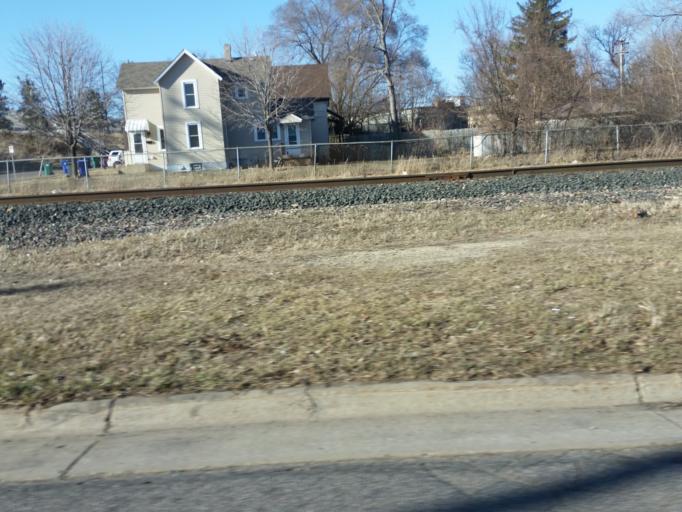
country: US
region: Minnesota
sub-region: Dakota County
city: West Saint Paul
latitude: 44.9324
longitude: -93.1181
